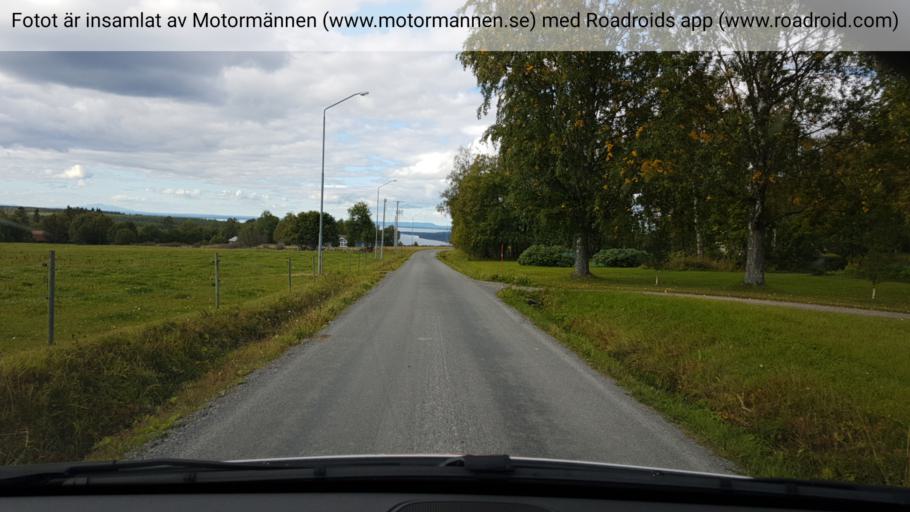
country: SE
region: Jaemtland
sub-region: OEstersunds Kommun
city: Ostersund
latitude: 63.1310
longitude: 14.5783
